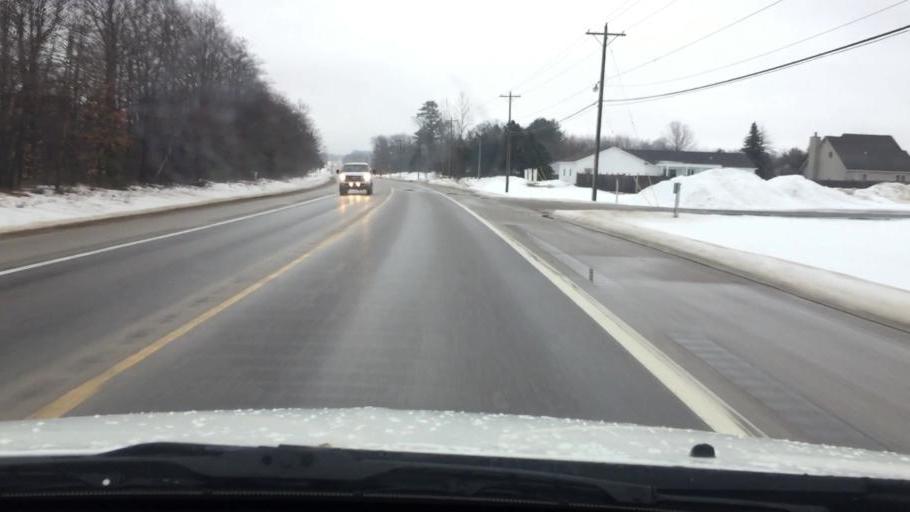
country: US
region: Michigan
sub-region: Charlevoix County
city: Charlevoix
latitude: 45.2823
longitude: -85.2378
